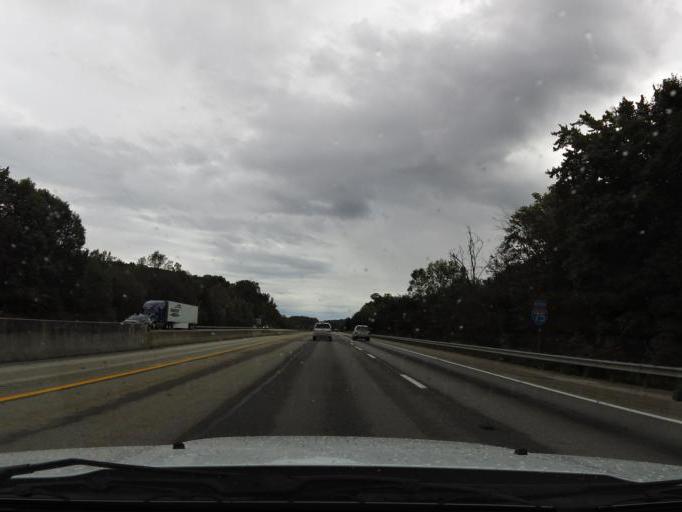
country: US
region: Kentucky
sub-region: Laurel County
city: London
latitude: 37.1538
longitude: -84.1123
